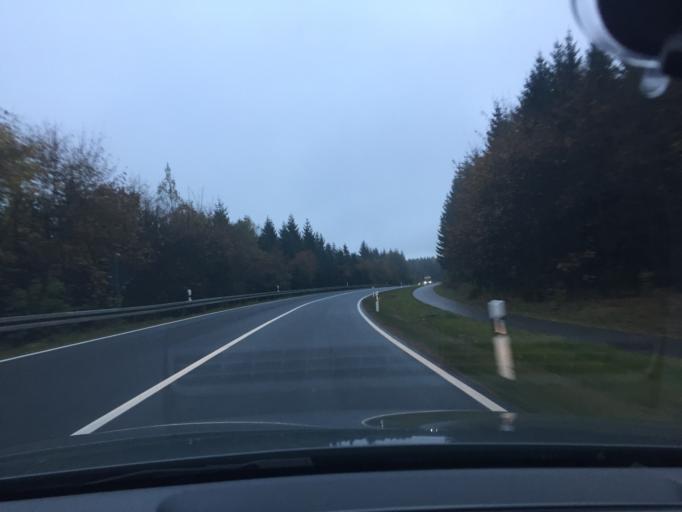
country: DE
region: Saxony
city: Altenberg
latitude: 50.7695
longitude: 13.7400
